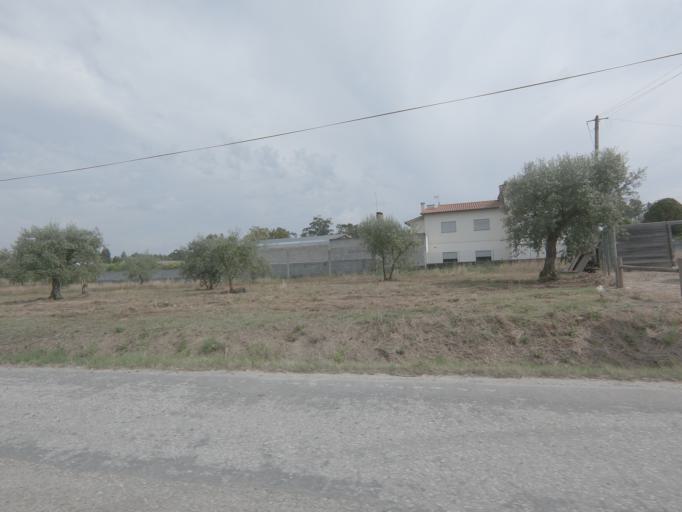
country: PT
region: Leiria
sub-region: Pombal
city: Pombal
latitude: 39.8828
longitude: -8.6748
